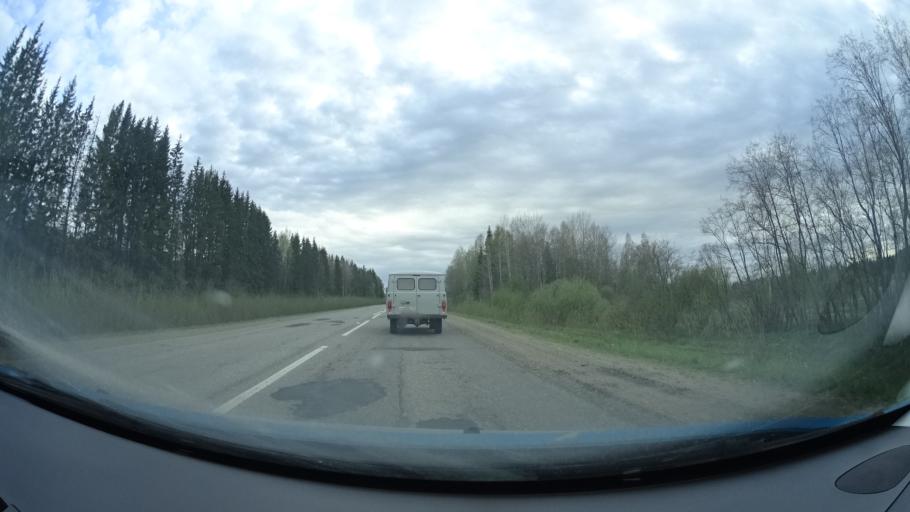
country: RU
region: Perm
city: Osa
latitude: 57.4471
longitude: 55.6476
